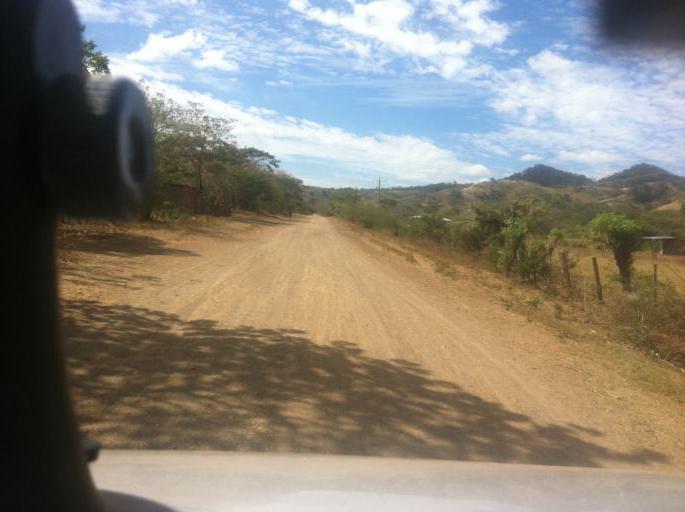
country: NI
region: Granada
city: Nandaime
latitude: 11.6302
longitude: -86.0182
